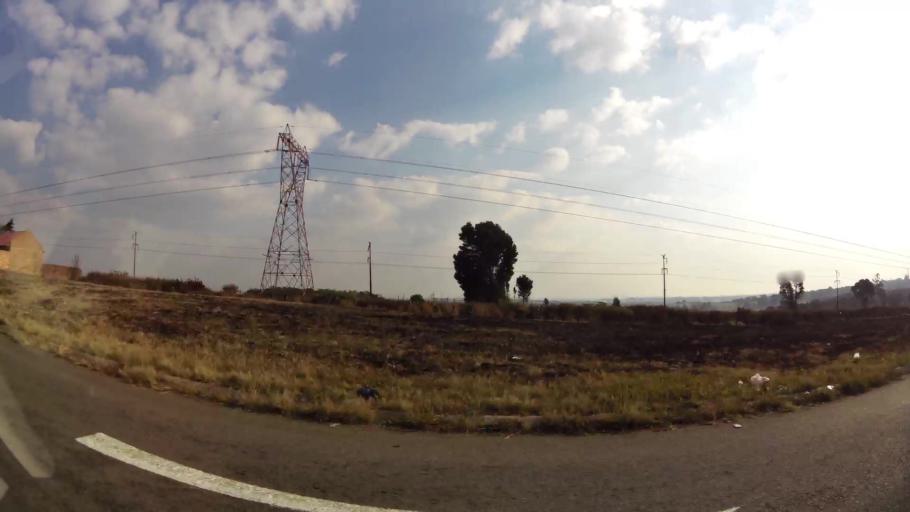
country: ZA
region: Gauteng
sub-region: City of Johannesburg Metropolitan Municipality
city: Modderfontein
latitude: -26.1045
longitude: 28.1857
